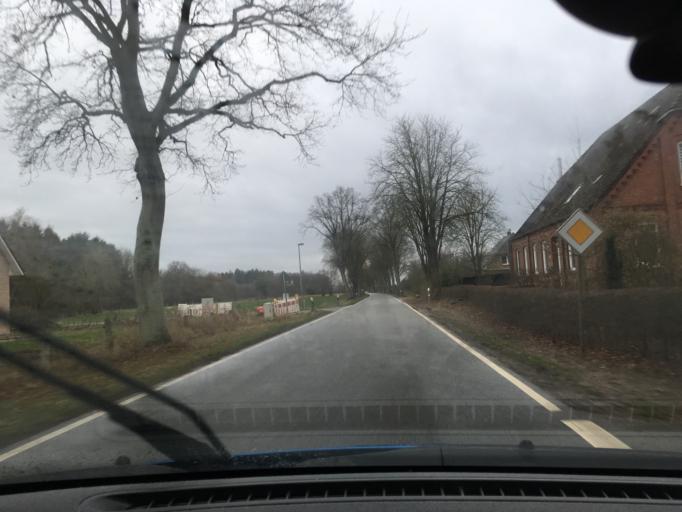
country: DE
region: Schleswig-Holstein
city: Lanze
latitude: 53.3641
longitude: 10.6151
